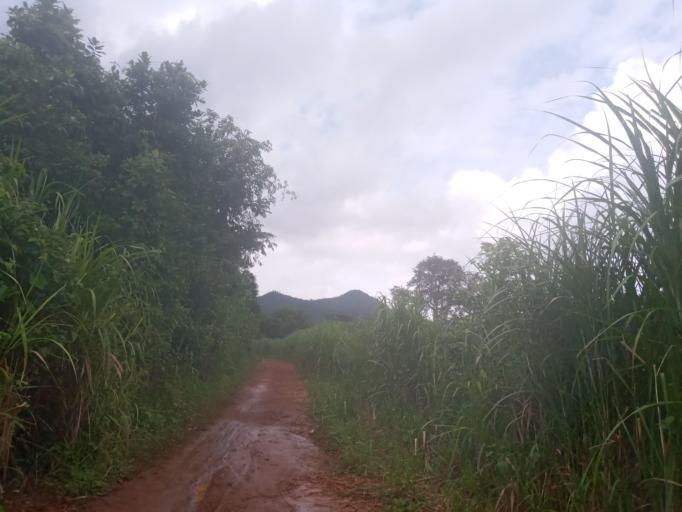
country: SL
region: Northern Province
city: Bumbuna
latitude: 8.9219
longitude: -11.7426
